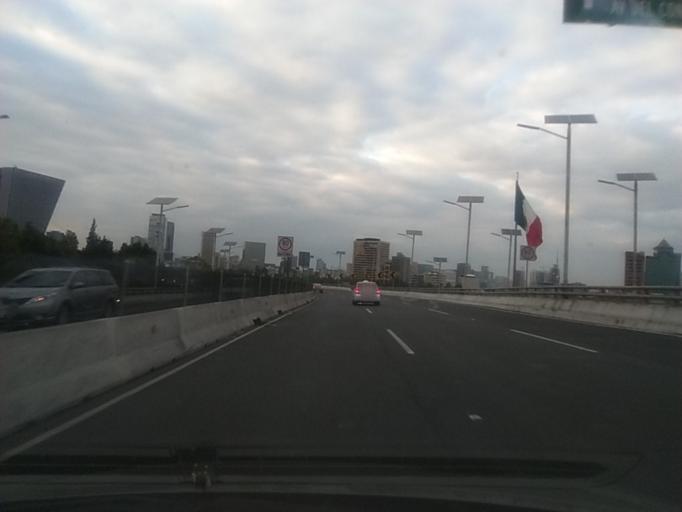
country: MX
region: Mexico City
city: Polanco
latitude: 19.4210
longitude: -99.1958
